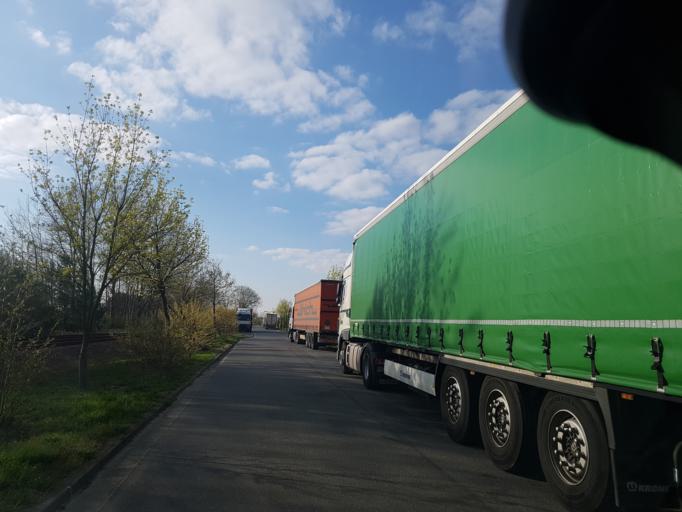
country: DE
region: Brandenburg
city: Bruck
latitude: 52.1774
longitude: 12.7745
